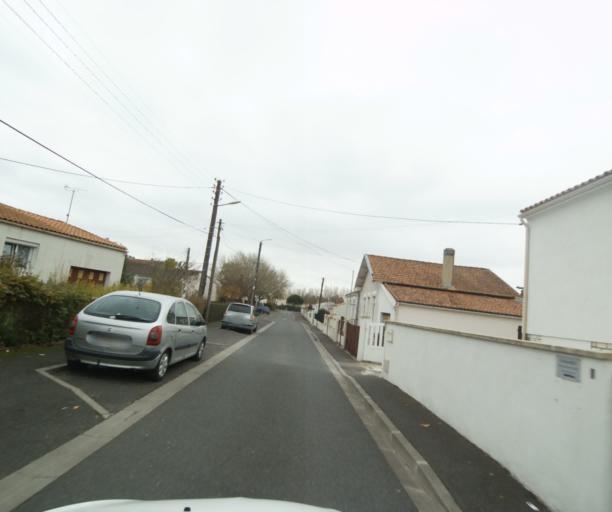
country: FR
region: Poitou-Charentes
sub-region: Departement de la Charente-Maritime
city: Saintes
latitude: 45.7353
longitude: -0.6186
